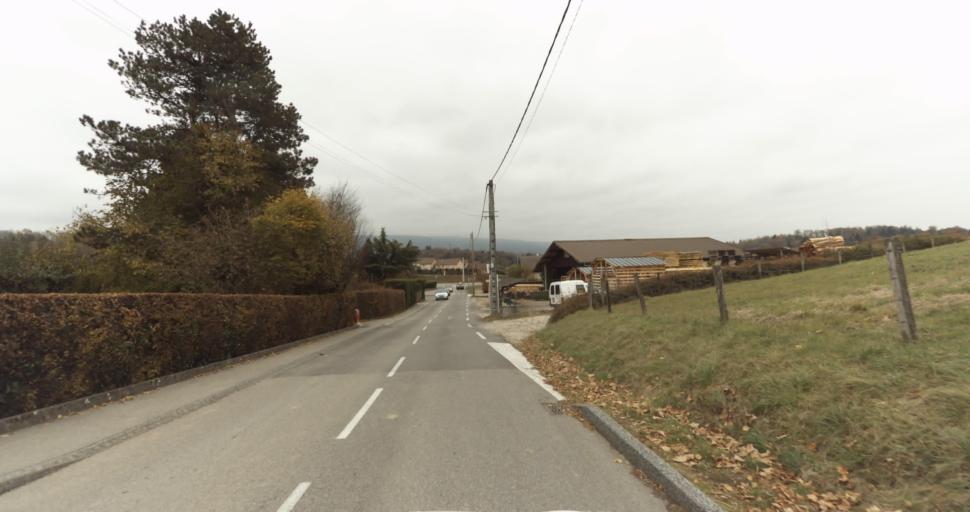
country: FR
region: Rhone-Alpes
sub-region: Departement de la Haute-Savoie
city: Chavanod
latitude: 45.8813
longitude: 6.0543
